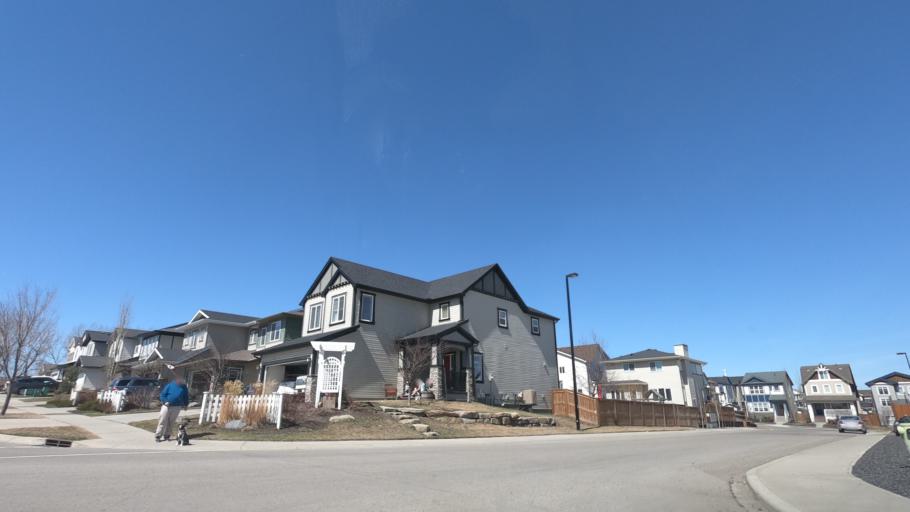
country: CA
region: Alberta
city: Airdrie
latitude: 51.3049
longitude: -114.0468
